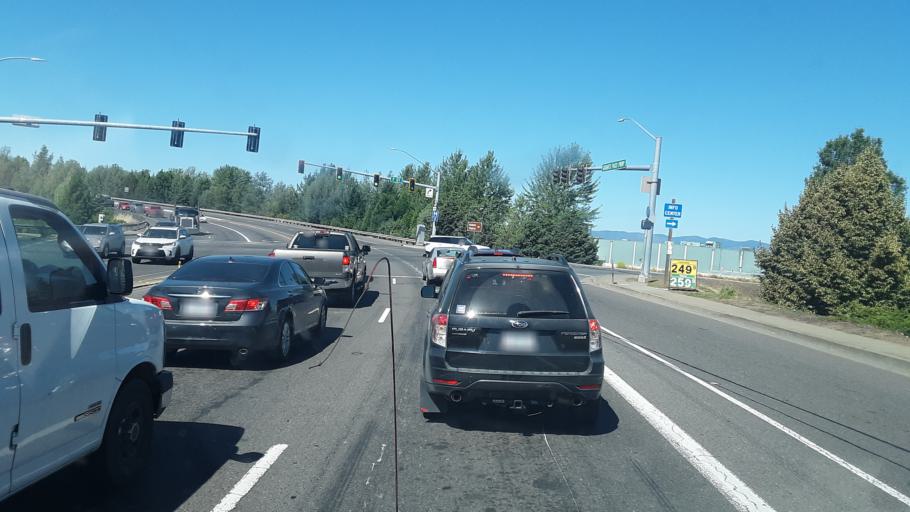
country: US
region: Oregon
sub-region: Josephine County
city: Fruitdale
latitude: 42.4371
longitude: -123.3097
